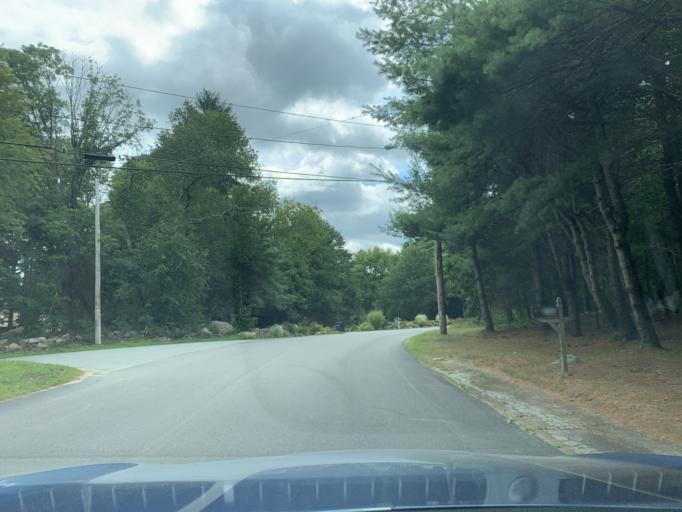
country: US
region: Rhode Island
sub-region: Kent County
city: West Warwick
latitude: 41.7426
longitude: -71.5800
